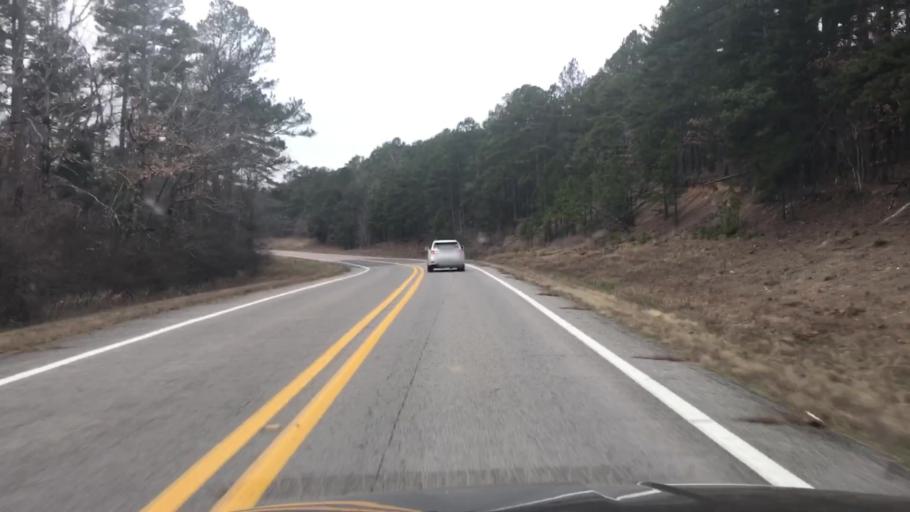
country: US
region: Arkansas
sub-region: Montgomery County
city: Mount Ida
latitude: 34.6868
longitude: -93.8754
